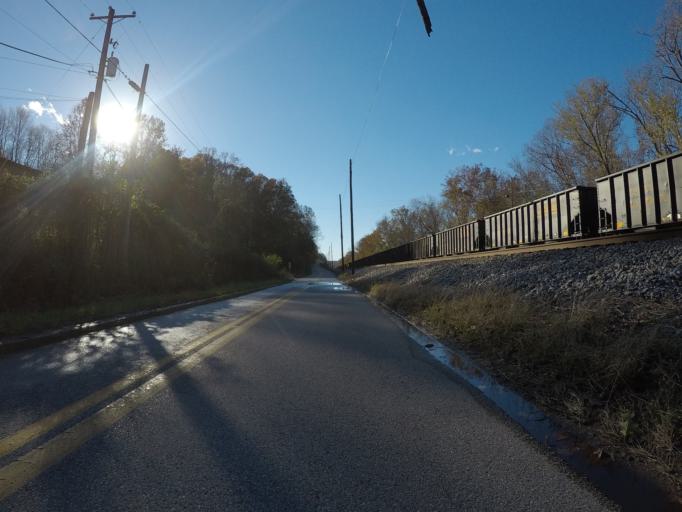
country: US
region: Ohio
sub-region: Lawrence County
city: Burlington
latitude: 38.3945
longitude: -82.5410
